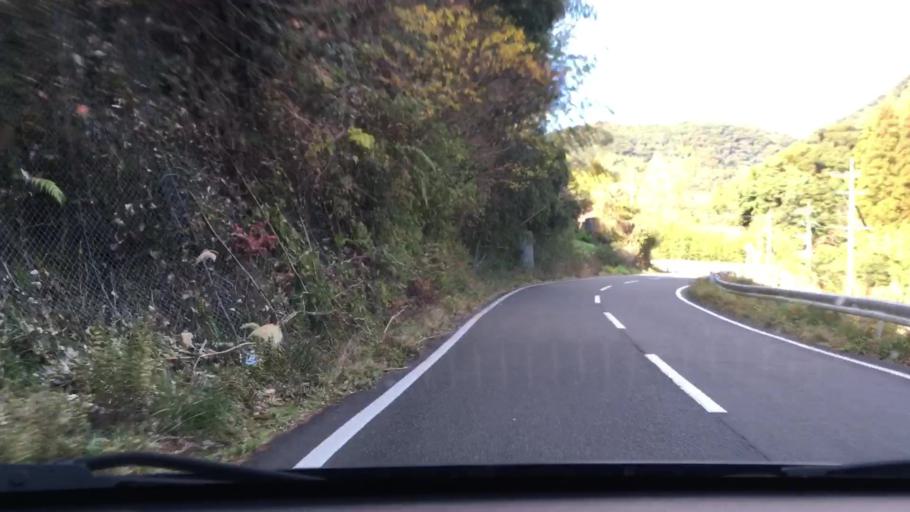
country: JP
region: Kagoshima
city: Ijuin
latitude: 31.7151
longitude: 130.4340
